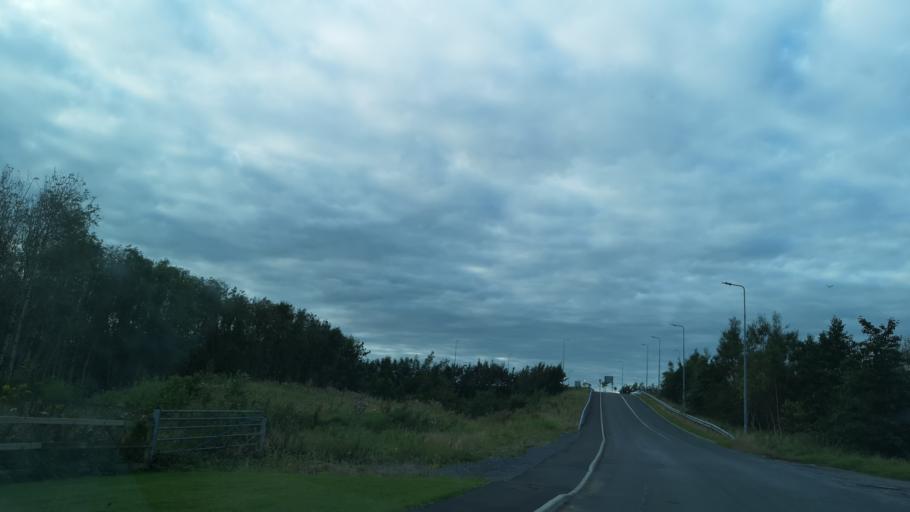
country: IE
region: Connaught
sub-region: County Galway
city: Athenry
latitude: 53.2883
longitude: -8.7550
